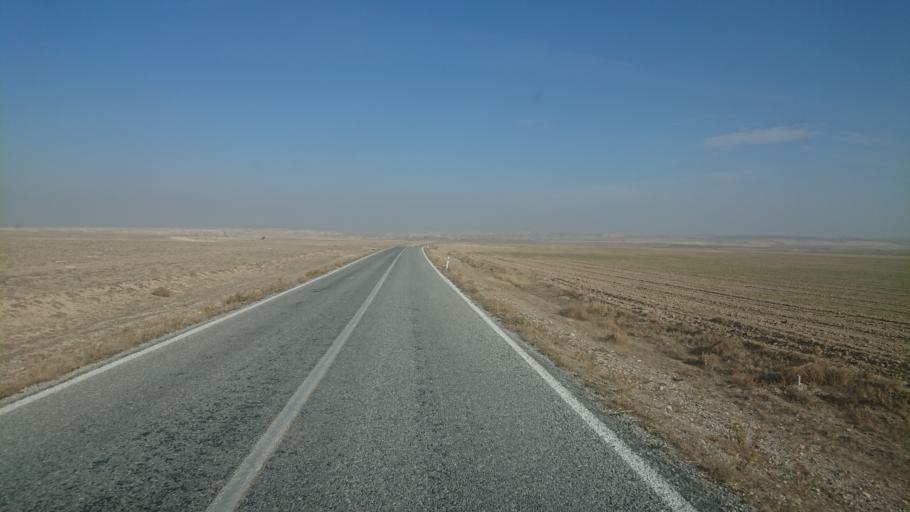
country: TR
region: Aksaray
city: Sultanhani
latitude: 38.0351
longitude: 33.5797
